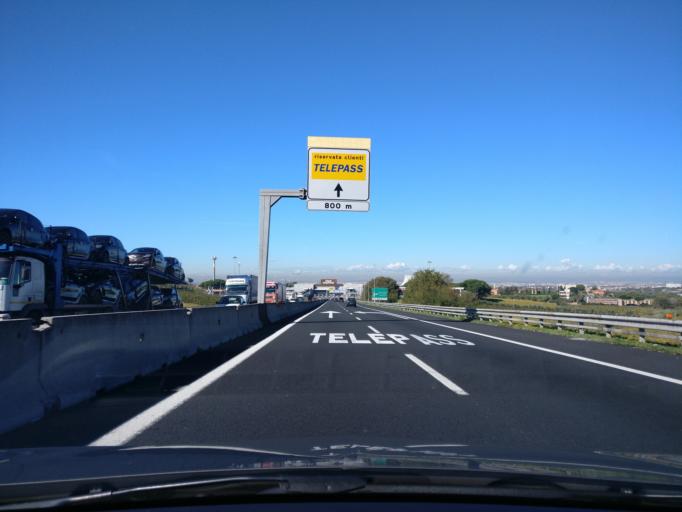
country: IT
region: Latium
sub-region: Citta metropolitana di Roma Capitale
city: Frascati
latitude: 41.8299
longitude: 12.6619
